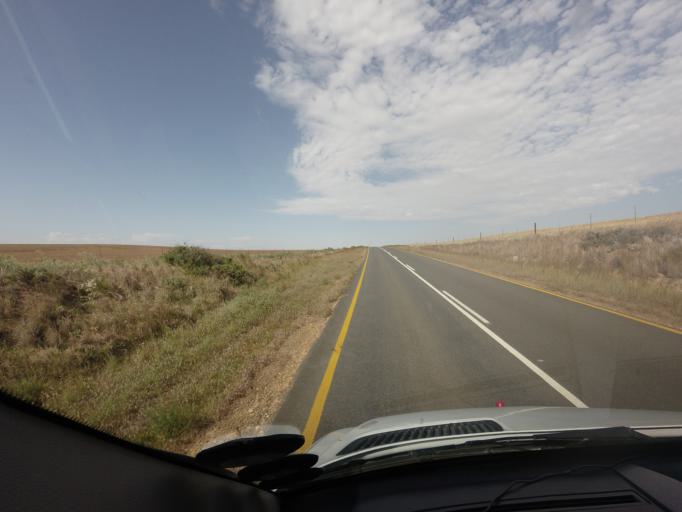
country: ZA
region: Western Cape
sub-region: Overberg District Municipality
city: Caledon
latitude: -34.3392
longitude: 19.6991
